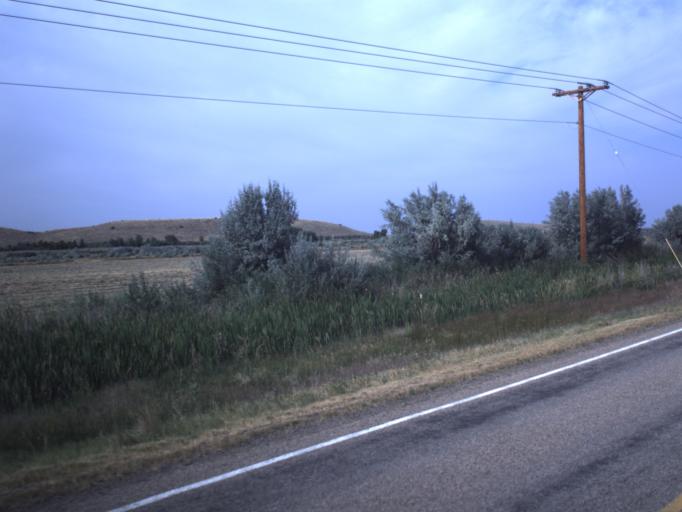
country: US
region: Utah
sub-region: Duchesne County
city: Roosevelt
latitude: 40.2580
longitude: -110.1813
